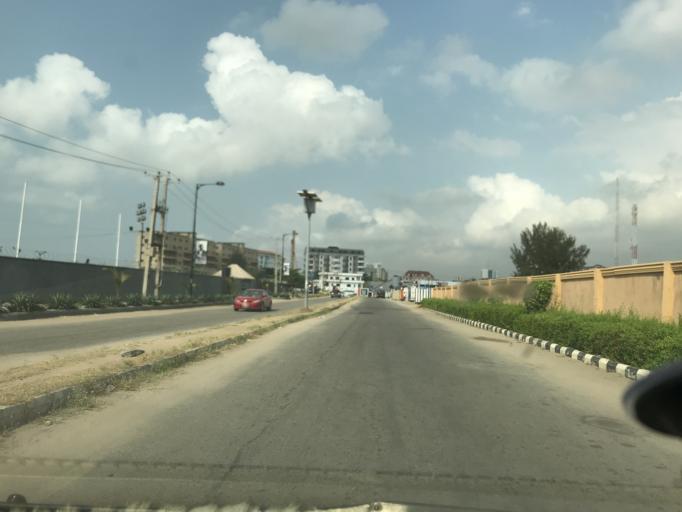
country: NG
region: Lagos
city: Ikoyi
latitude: 6.4242
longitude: 3.4433
